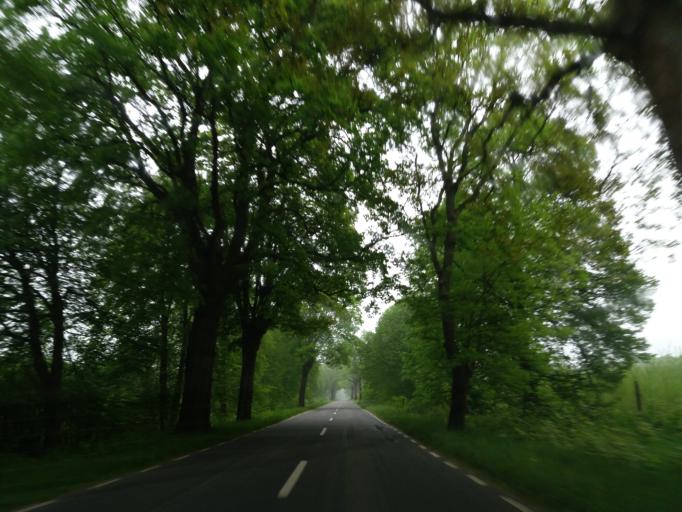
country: PL
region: West Pomeranian Voivodeship
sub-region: Powiat choszczenski
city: Drawno
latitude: 53.2263
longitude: 15.7905
